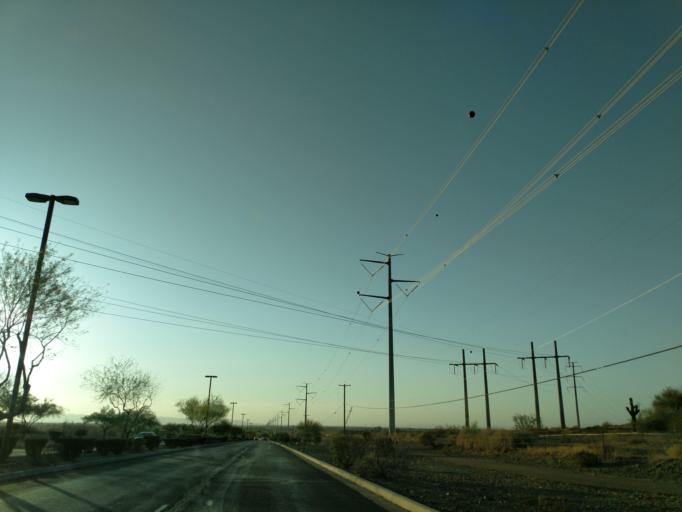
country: US
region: Arizona
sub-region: Maricopa County
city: Laveen
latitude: 33.3207
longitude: -112.1649
